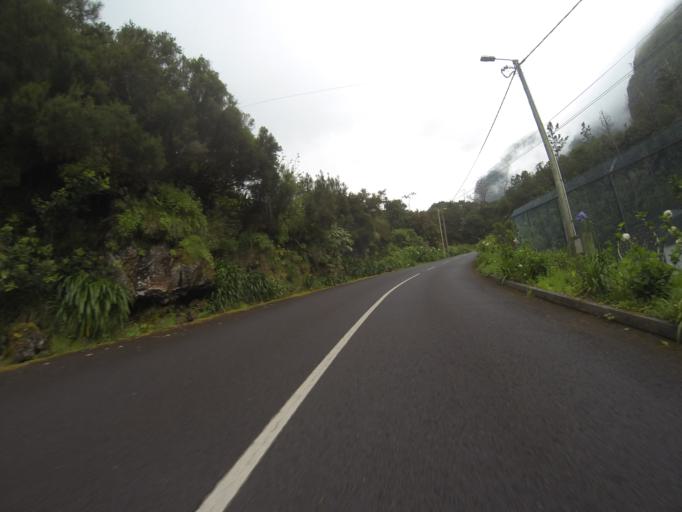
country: PT
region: Madeira
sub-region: Porto Moniz
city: Porto Moniz
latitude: 32.8132
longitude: -17.1117
